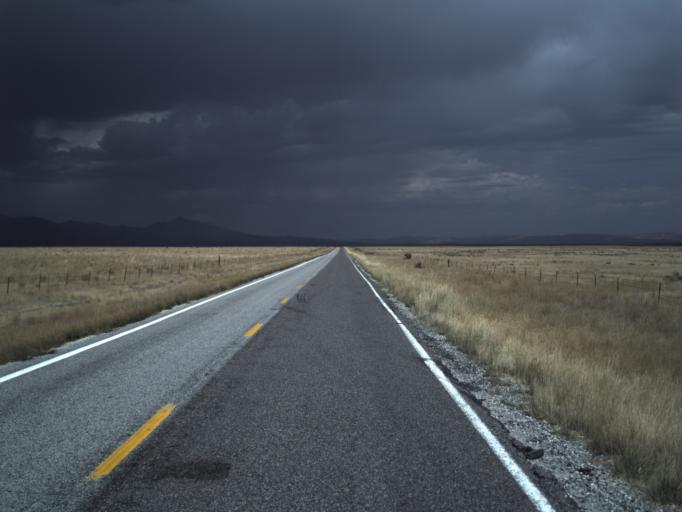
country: US
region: Idaho
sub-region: Oneida County
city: Malad City
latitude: 41.8718
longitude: -113.1225
